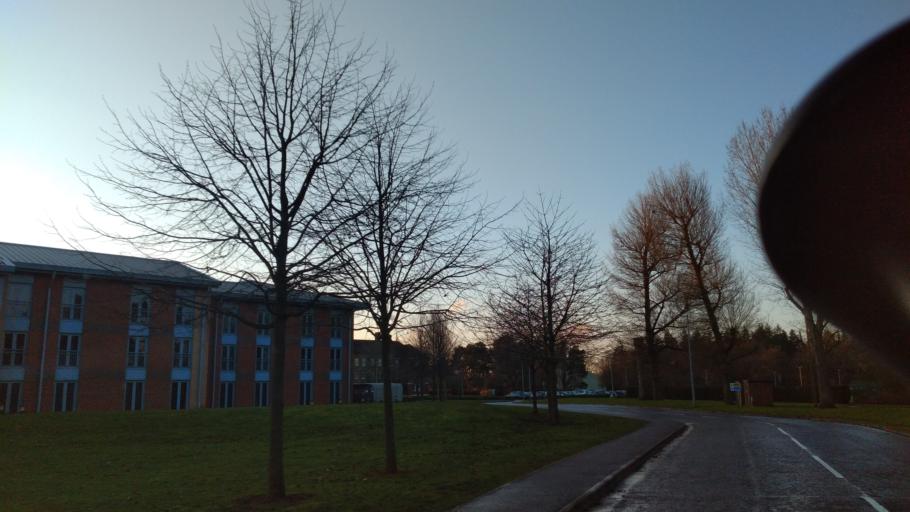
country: GB
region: England
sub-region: Oxfordshire
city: Shrivenham
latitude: 51.6110
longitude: -1.6379
